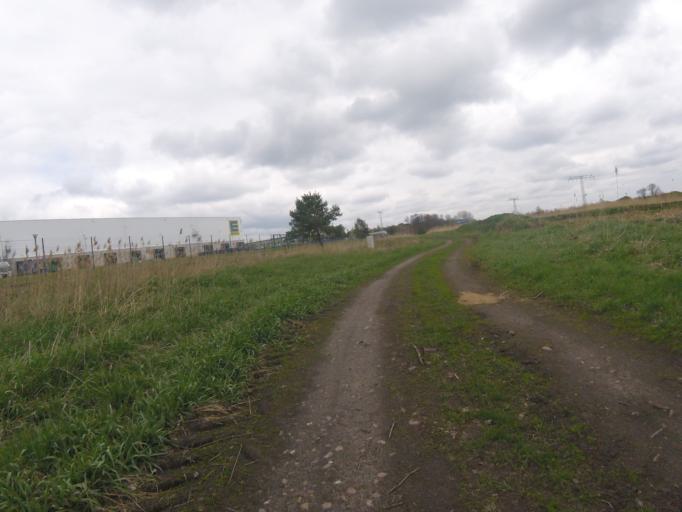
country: DE
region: Brandenburg
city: Mittenwalde
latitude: 52.2591
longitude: 13.5748
